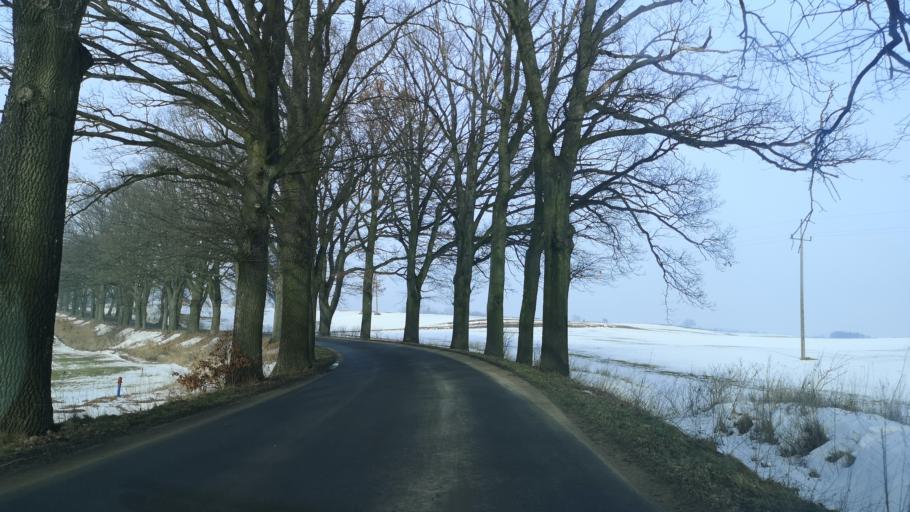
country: PL
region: Warmian-Masurian Voivodeship
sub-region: Powiat nowomiejski
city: Biskupiec
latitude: 53.5128
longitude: 19.3510
